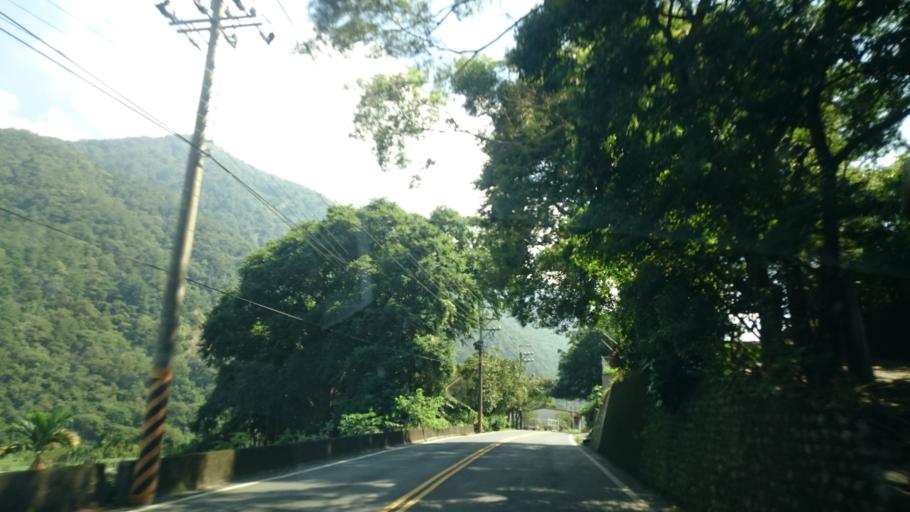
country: TW
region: Taiwan
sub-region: Nantou
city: Puli
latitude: 23.9881
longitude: 121.0199
